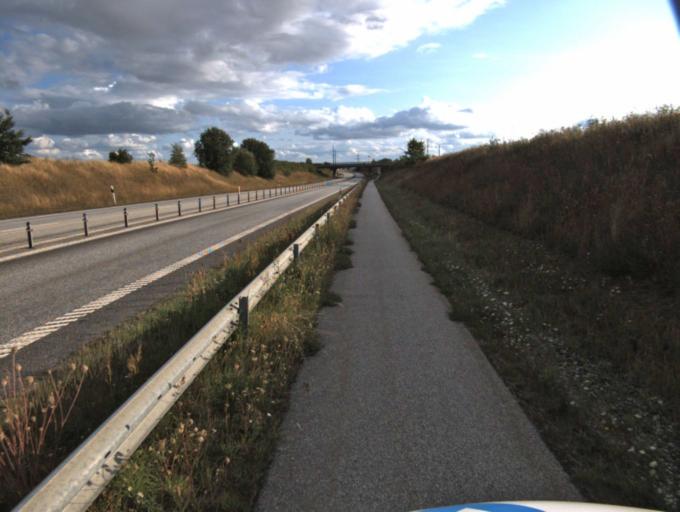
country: SE
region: Skane
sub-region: Kavlinge Kommun
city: Kaevlinge
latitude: 55.7645
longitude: 13.1314
